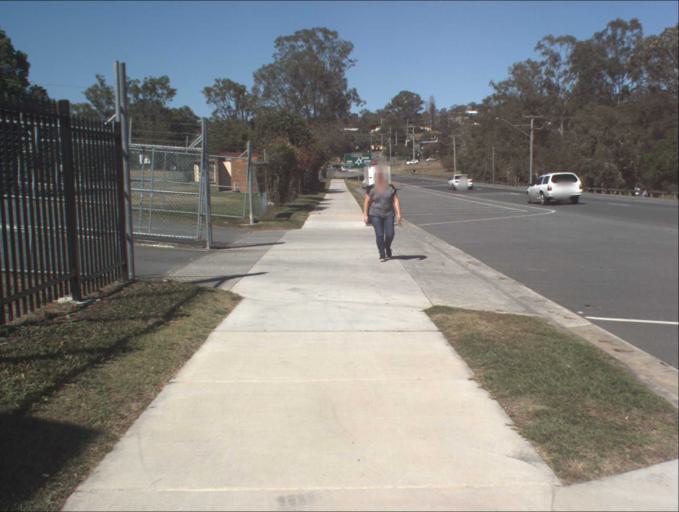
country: AU
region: Queensland
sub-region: Logan
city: Beenleigh
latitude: -27.7200
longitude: 153.1971
